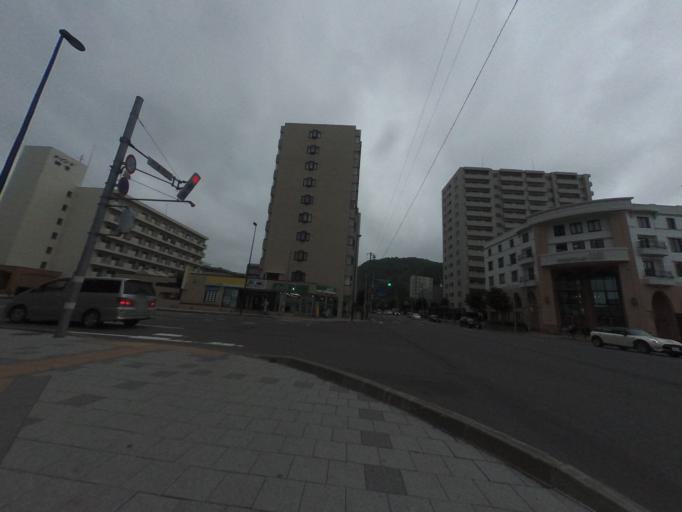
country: JP
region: Hokkaido
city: Sapporo
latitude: 43.0555
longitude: 141.3160
